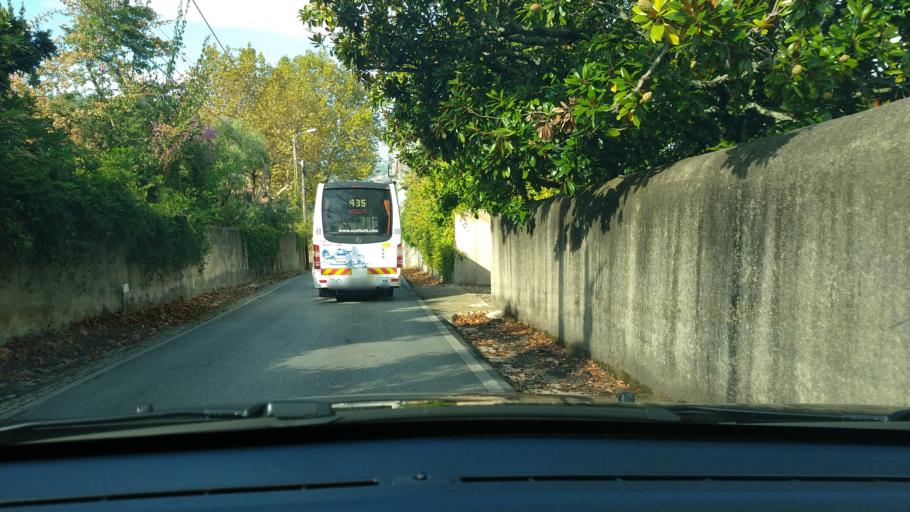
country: PT
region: Lisbon
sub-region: Sintra
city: Colares
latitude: 38.7950
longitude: -9.4293
